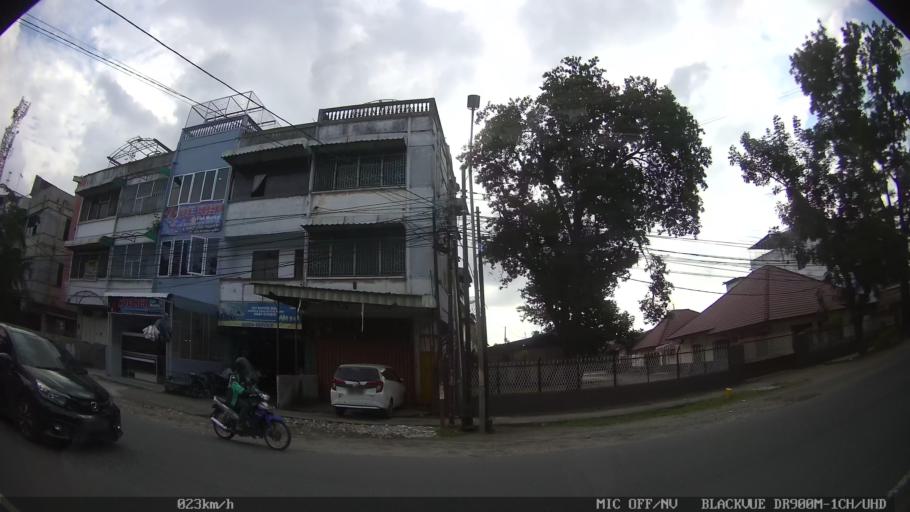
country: ID
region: North Sumatra
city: Medan
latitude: 3.6121
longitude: 98.6735
